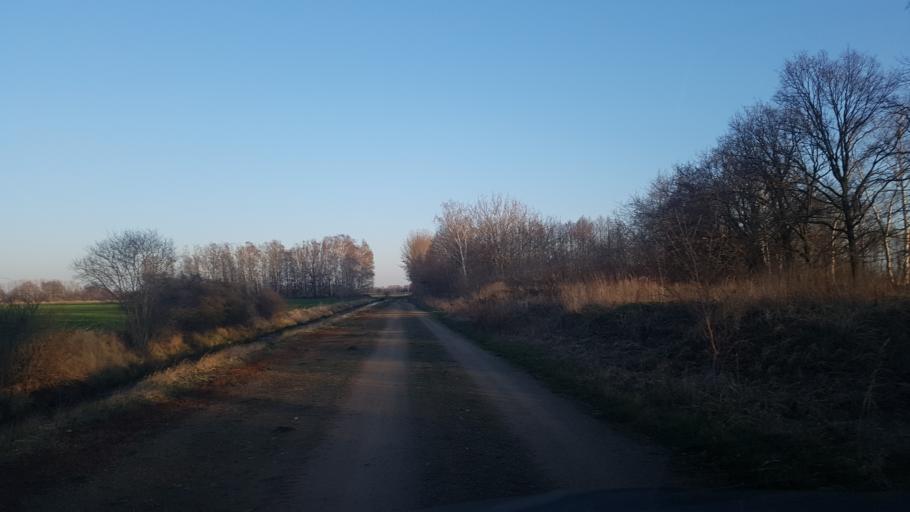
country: DE
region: Brandenburg
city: Bad Liebenwerda
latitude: 51.5295
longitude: 13.3536
